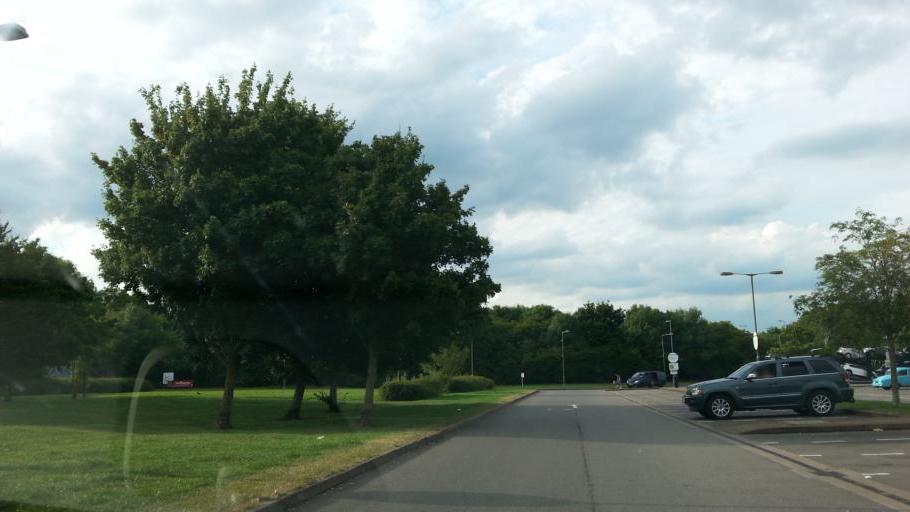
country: GB
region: England
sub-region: Worcestershire
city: Bredon
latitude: 52.0652
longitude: -2.1586
